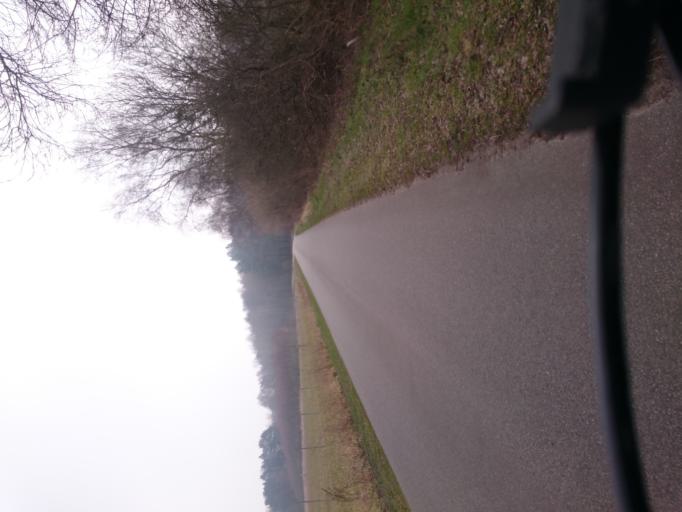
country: DE
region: Mecklenburg-Vorpommern
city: Barth
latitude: 54.3683
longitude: 12.6611
